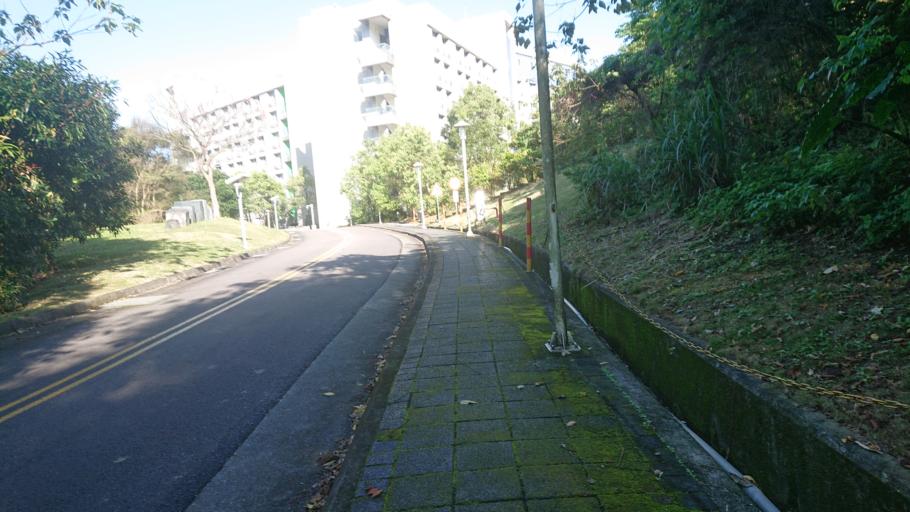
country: TW
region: Taipei
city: Taipei
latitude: 24.9793
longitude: 121.5731
